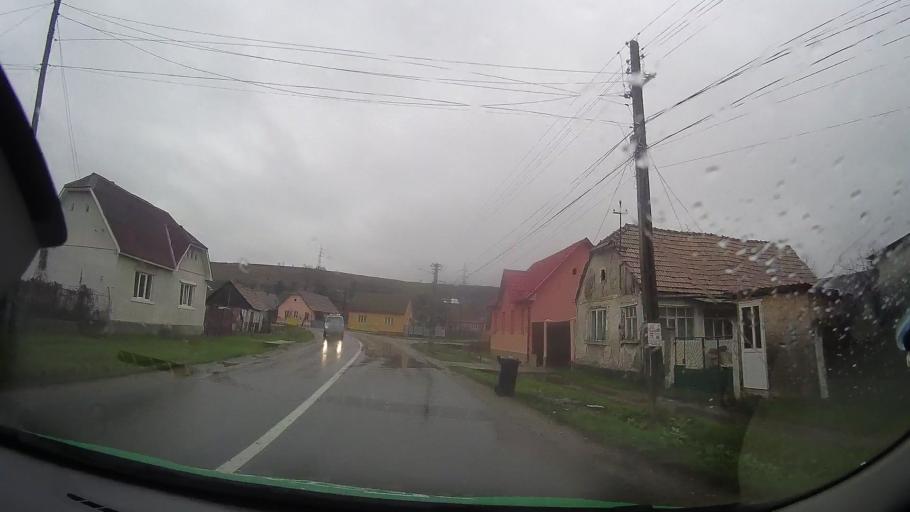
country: RO
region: Bistrita-Nasaud
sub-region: Comuna Mariselu
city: Mariselu
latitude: 47.0395
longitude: 24.4742
